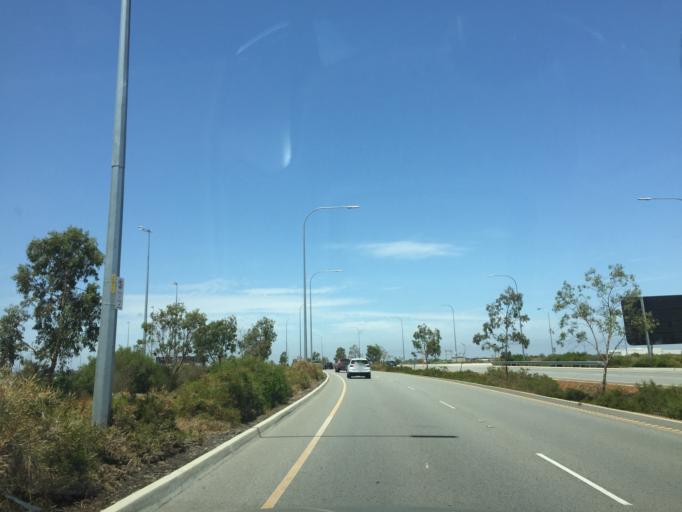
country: AU
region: Western Australia
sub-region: Belmont
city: Redcliffe
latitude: -31.9490
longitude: 115.9718
